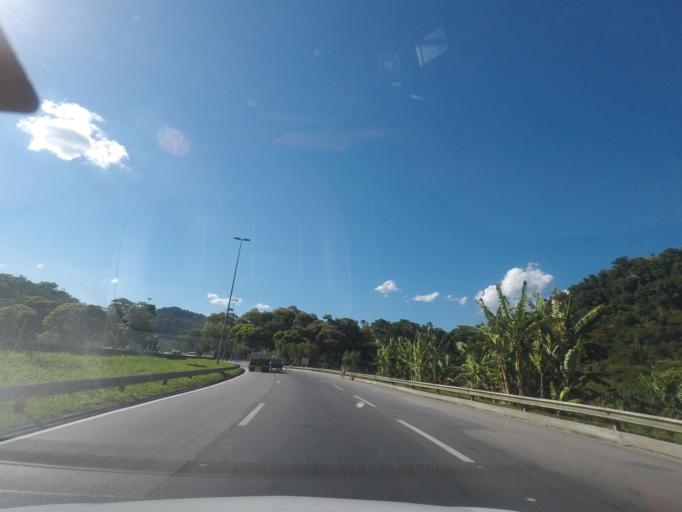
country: BR
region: Rio de Janeiro
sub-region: Petropolis
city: Petropolis
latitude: -22.6588
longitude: -43.1169
